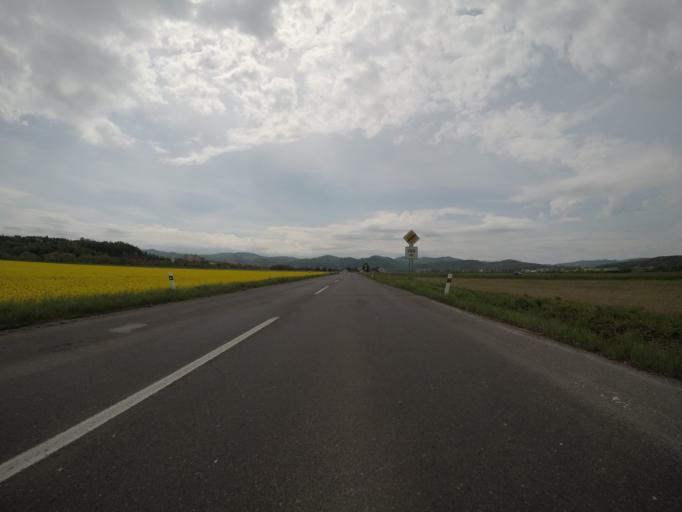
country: SK
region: Banskobystricky
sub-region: Okres Banska Bystrica
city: Zvolen
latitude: 48.6037
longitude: 19.1255
